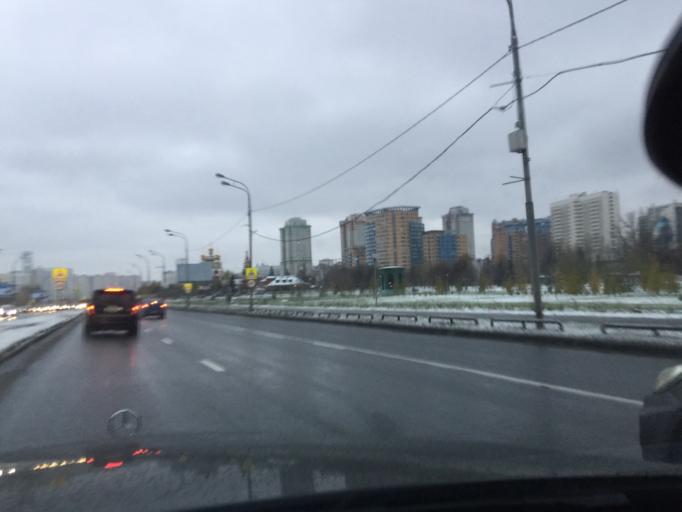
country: RU
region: Moscow
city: Troparevo
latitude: 55.6587
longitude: 37.4811
